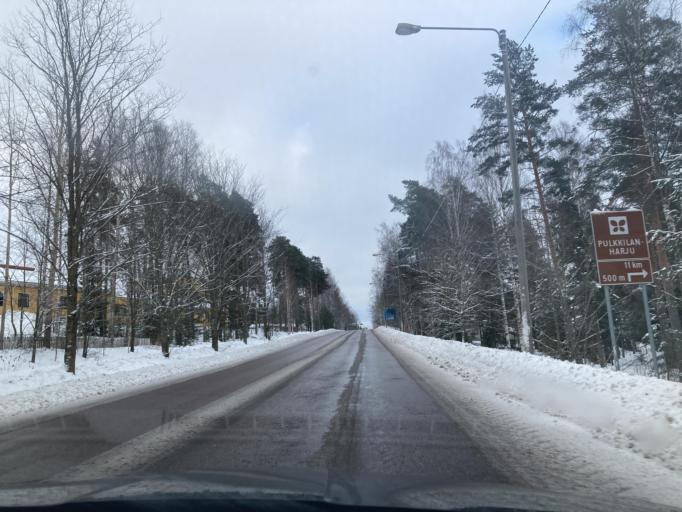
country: FI
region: Paijanne Tavastia
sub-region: Lahti
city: Asikkala
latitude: 61.1721
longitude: 25.5397
